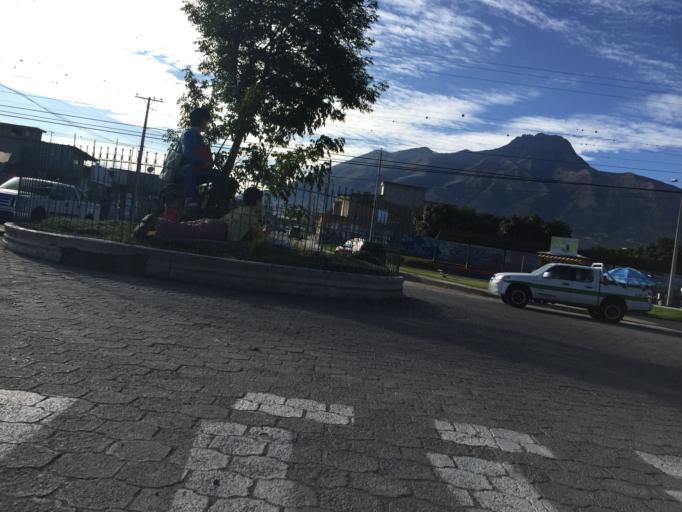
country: EC
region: Imbabura
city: Atuntaqui
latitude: 0.3351
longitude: -78.2116
